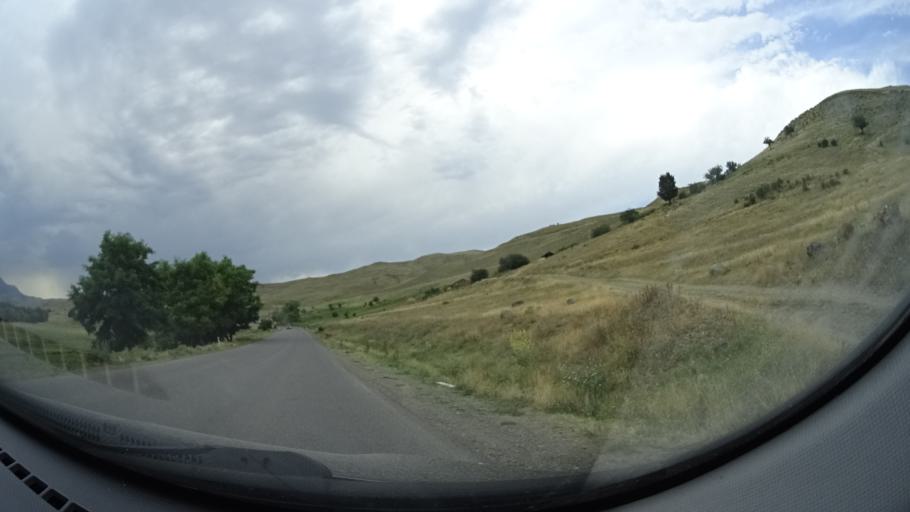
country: GE
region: Samtskhe-Javakheti
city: Aspindza
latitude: 41.5948
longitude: 43.2265
